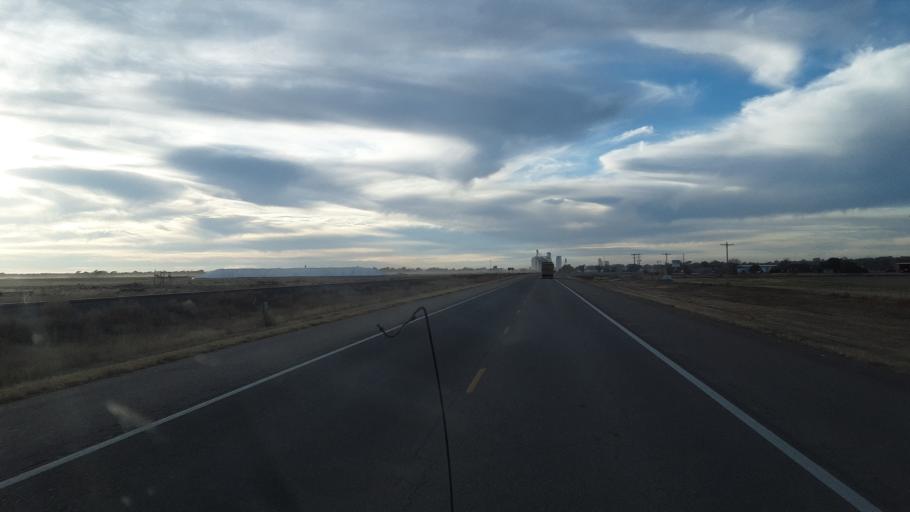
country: US
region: Kansas
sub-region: Hamilton County
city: Syracuse
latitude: 37.9737
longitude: -101.7292
